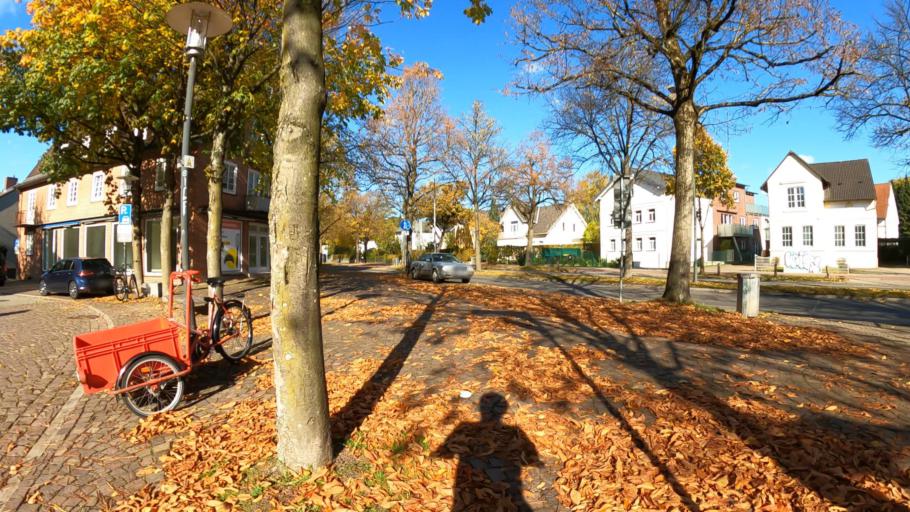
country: DE
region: Schleswig-Holstein
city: Ahrensburg
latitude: 53.6692
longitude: 10.2432
